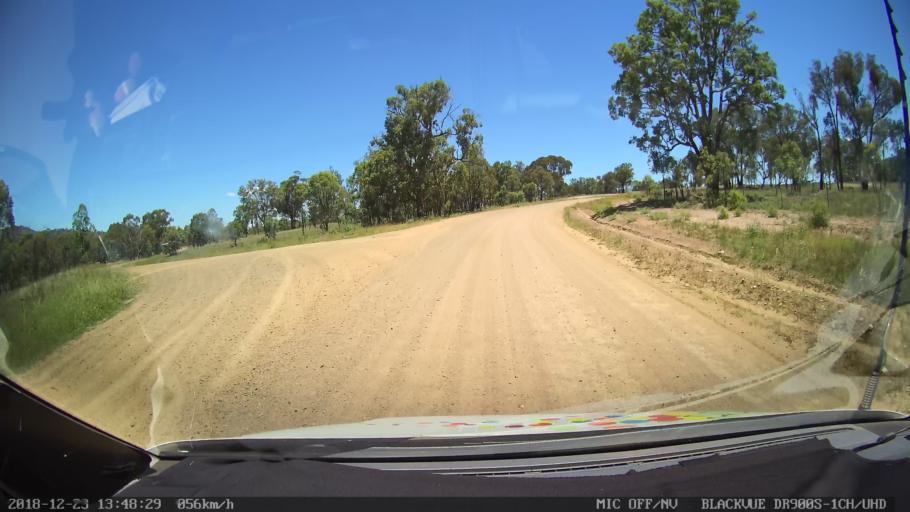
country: AU
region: New South Wales
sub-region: Tamworth Municipality
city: Manilla
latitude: -30.5179
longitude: 151.1164
